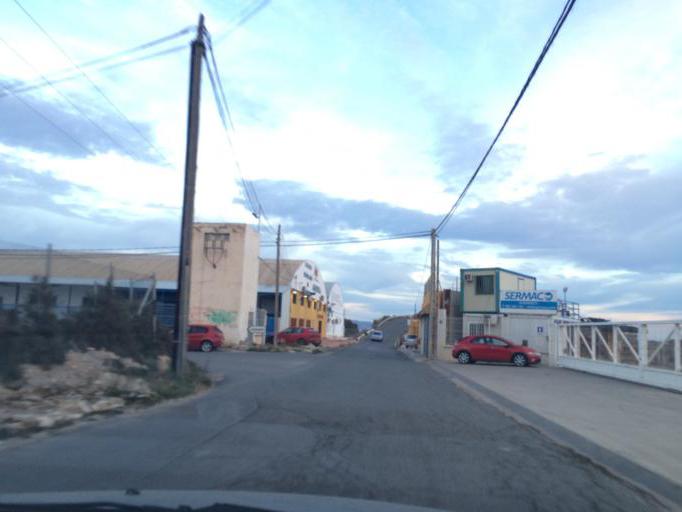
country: ES
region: Andalusia
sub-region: Provincia de Almeria
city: Viator
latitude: 36.8448
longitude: -2.4005
